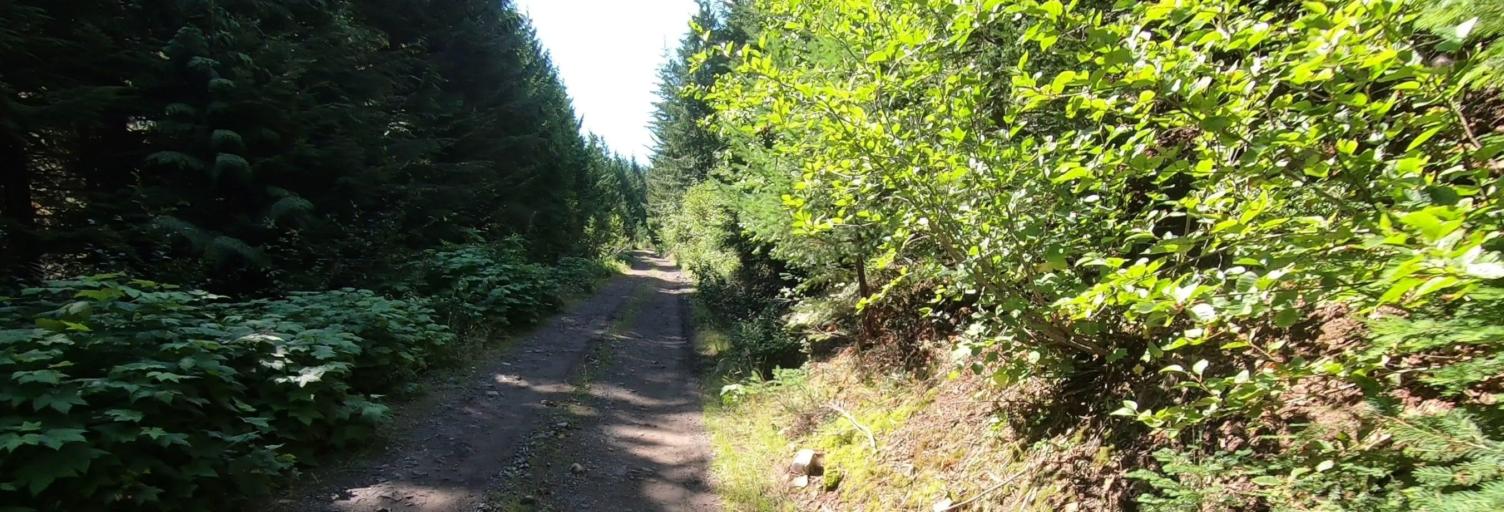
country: CA
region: British Columbia
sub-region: Fraser Valley Regional District
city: Chilliwack
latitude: 48.8601
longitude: -121.7796
